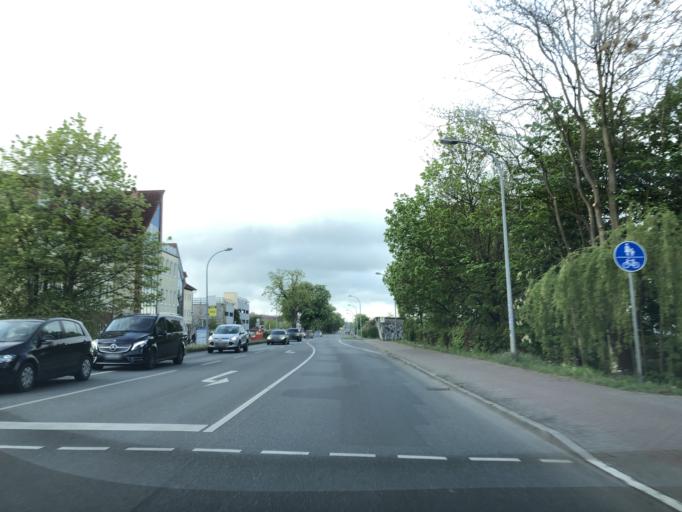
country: DE
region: Mecklenburg-Vorpommern
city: Guestrow
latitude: 53.7812
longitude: 12.1761
